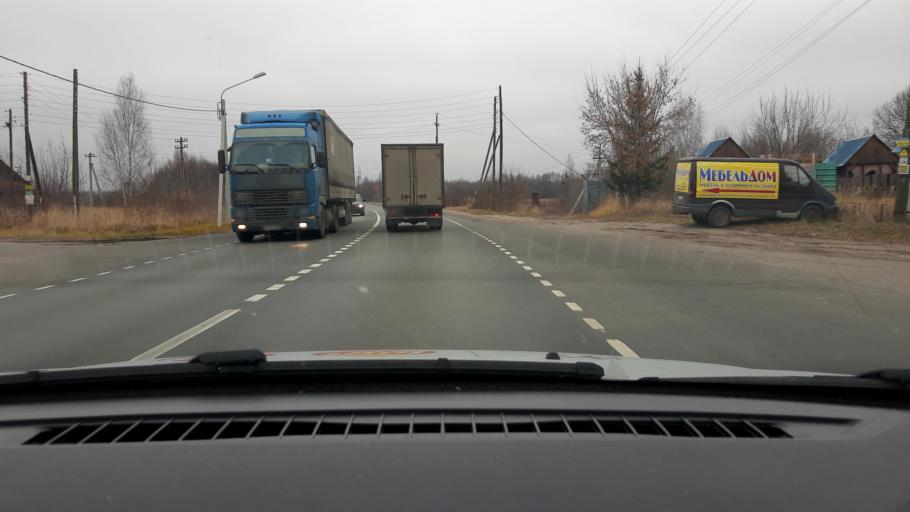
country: RU
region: Nizjnij Novgorod
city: Gorodets
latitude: 56.6089
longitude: 43.4450
